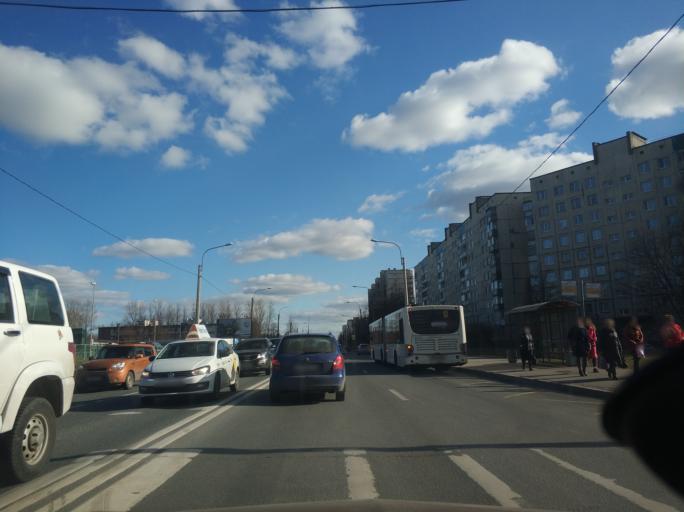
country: RU
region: St.-Petersburg
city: Krasnogvargeisky
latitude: 59.9569
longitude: 30.4938
